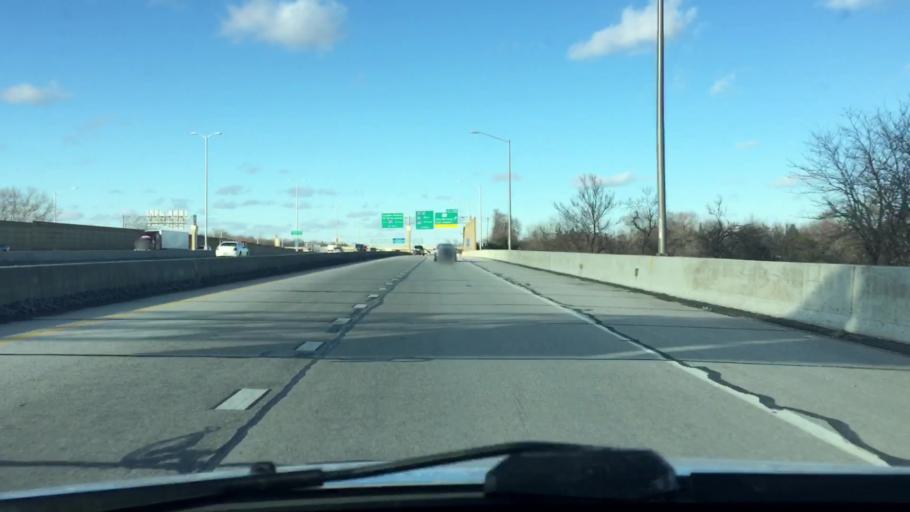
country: US
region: Wisconsin
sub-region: Milwaukee County
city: Greendale
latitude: 42.9355
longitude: -87.9349
